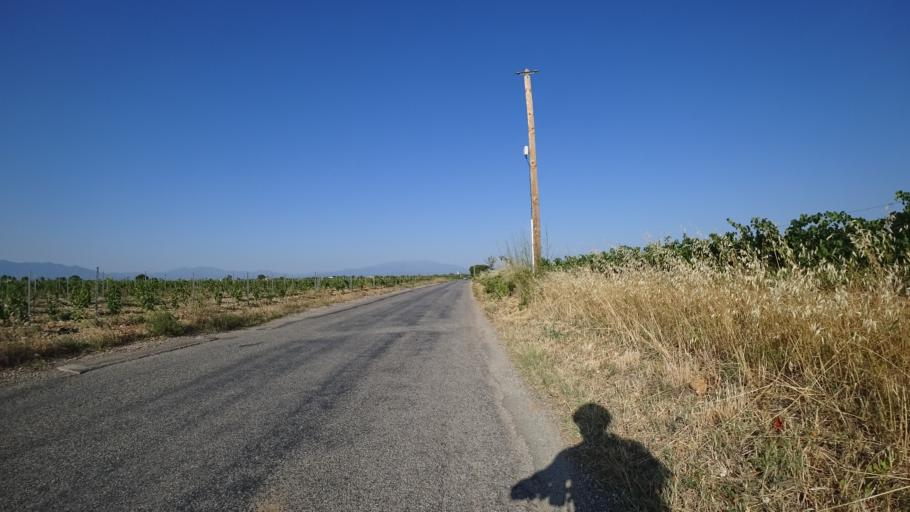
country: FR
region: Languedoc-Roussillon
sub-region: Departement des Pyrenees-Orientales
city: Cabestany
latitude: 42.6866
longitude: 2.9612
